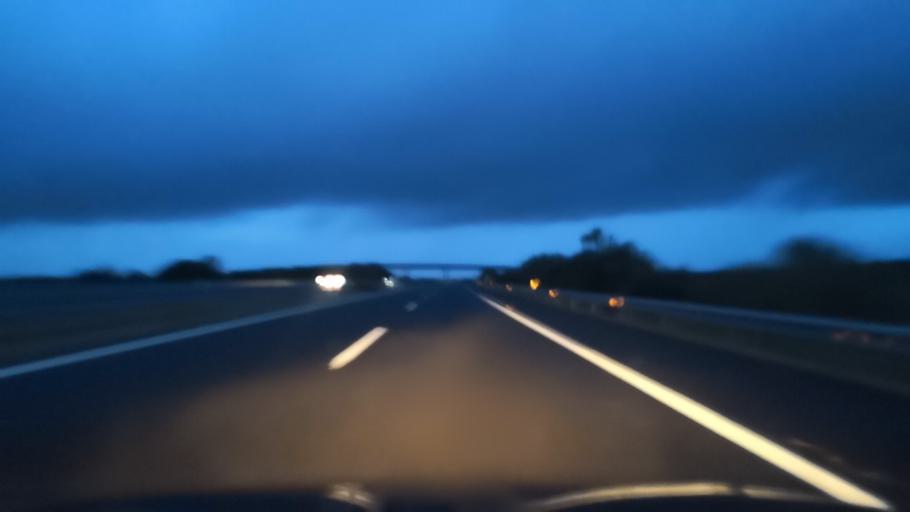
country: ES
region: Extremadura
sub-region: Provincia de Caceres
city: Aldea del Cano
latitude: 39.3248
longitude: -6.3304
